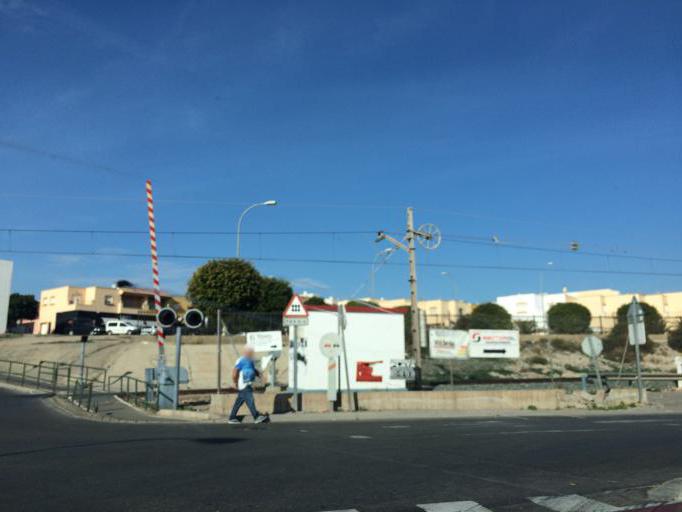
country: ES
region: Andalusia
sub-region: Provincia de Almeria
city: Almeria
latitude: 36.8479
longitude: -2.4344
